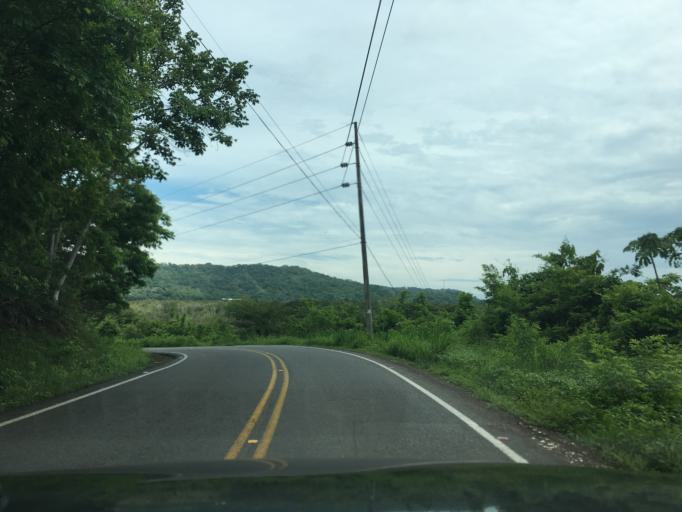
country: CR
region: Puntarenas
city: Esparza
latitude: 9.9335
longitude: -84.6935
